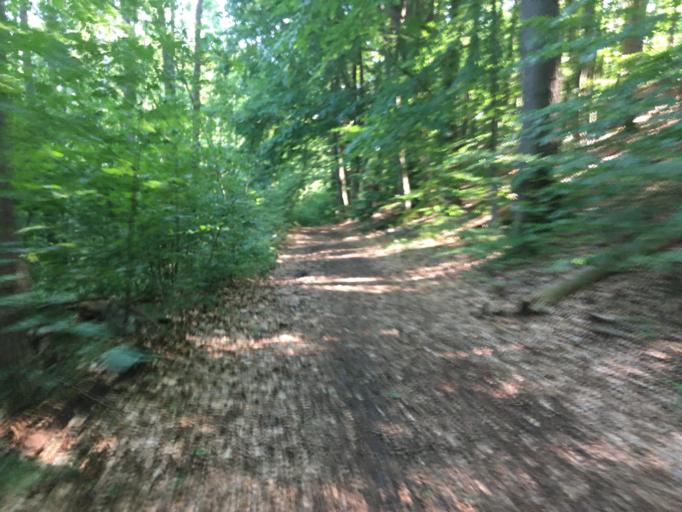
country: DE
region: Brandenburg
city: Templin
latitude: 53.1280
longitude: 13.5572
